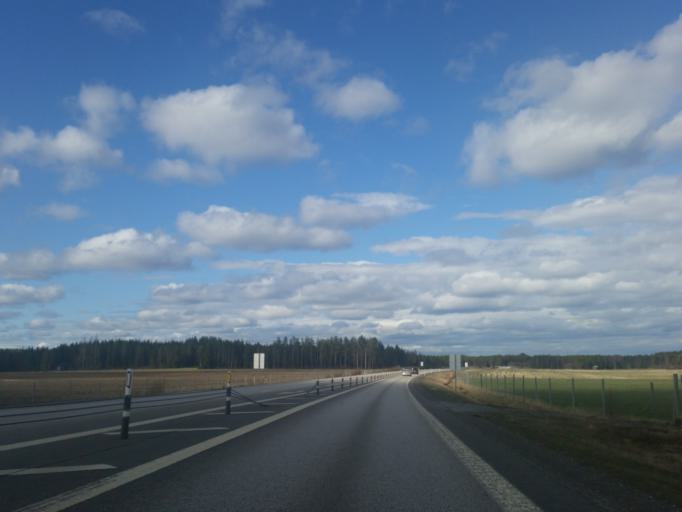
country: SE
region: Vaesterbotten
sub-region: Robertsfors Kommun
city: Robertsfors
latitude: 64.1016
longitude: 20.8708
